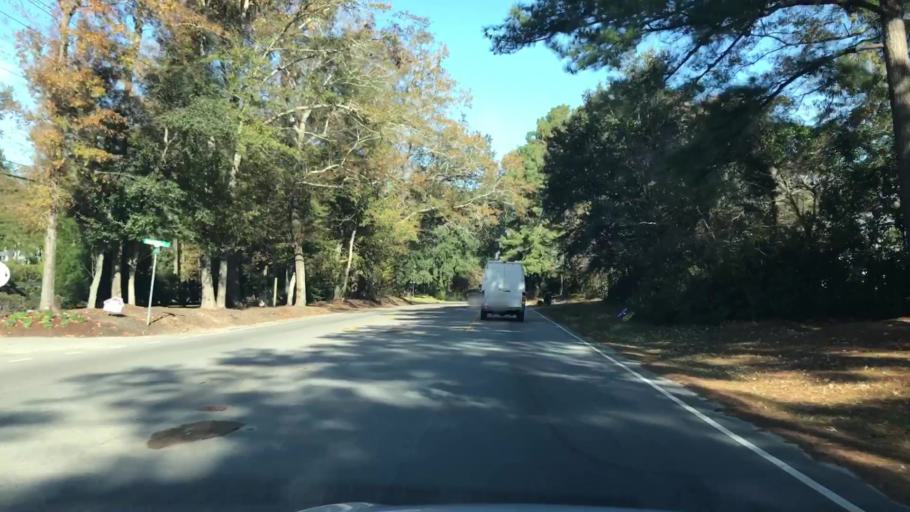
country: US
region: South Carolina
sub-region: Dorchester County
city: Summerville
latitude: 33.0147
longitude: -80.2388
